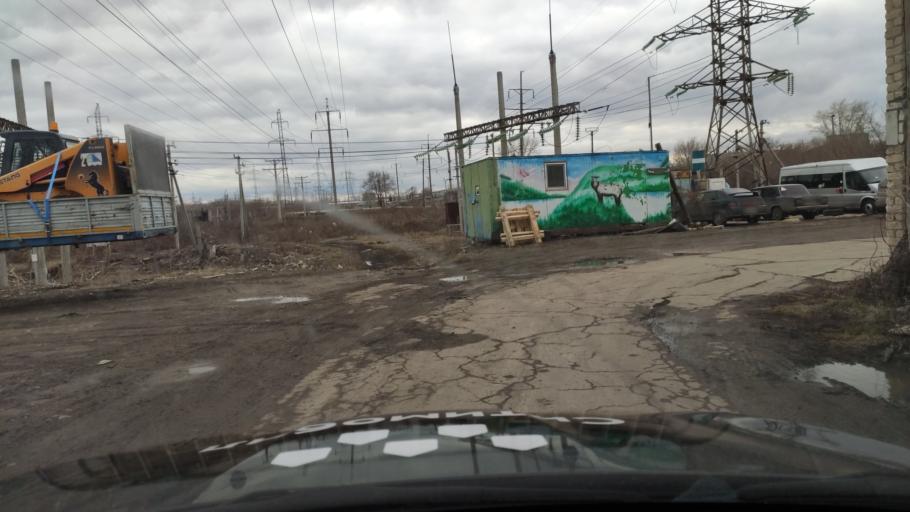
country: RU
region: Samara
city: Tol'yatti
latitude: 53.5265
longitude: 49.4688
